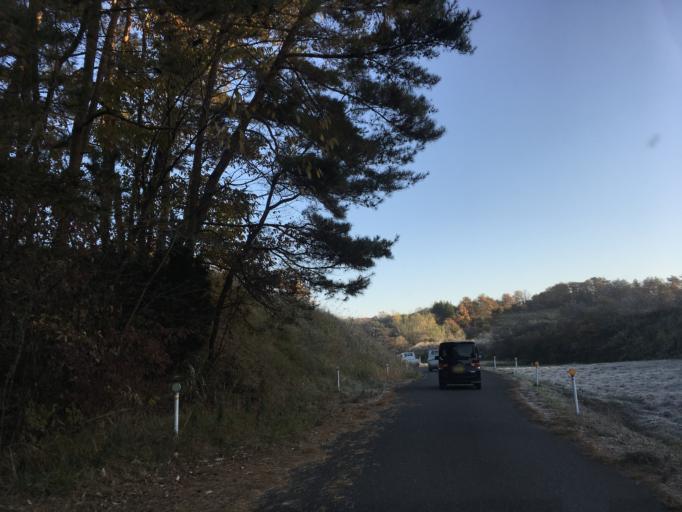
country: JP
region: Iwate
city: Ichinoseki
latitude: 38.7943
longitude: 141.2134
